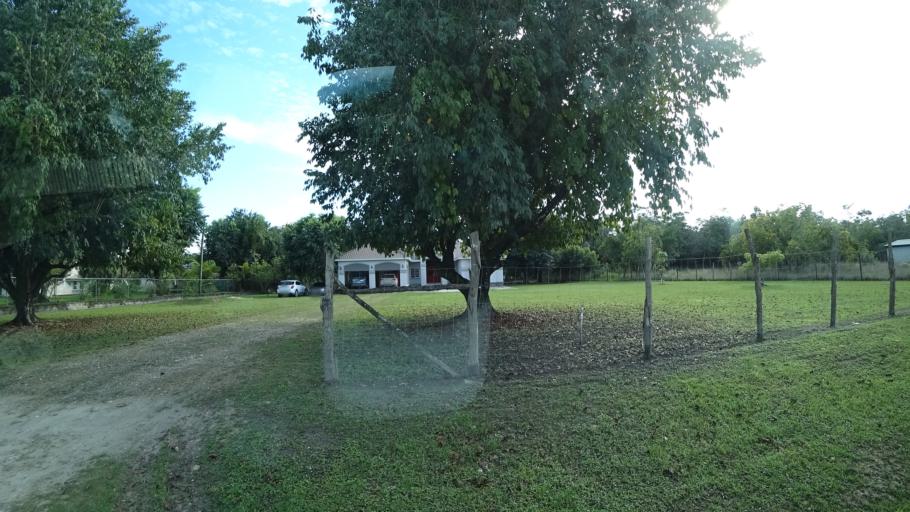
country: BZ
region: Belize
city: Belize City
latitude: 17.5566
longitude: -88.4040
